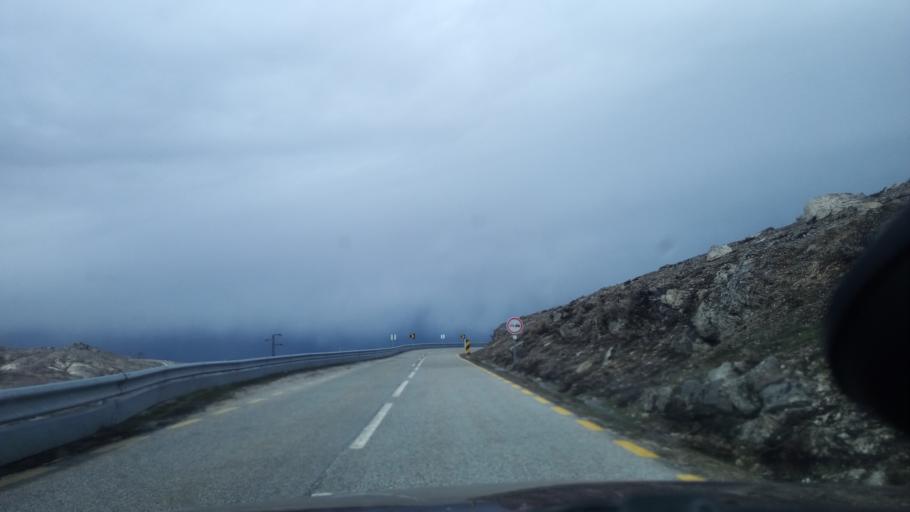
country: PT
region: Guarda
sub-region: Manteigas
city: Manteigas
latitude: 40.4188
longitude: -7.6160
